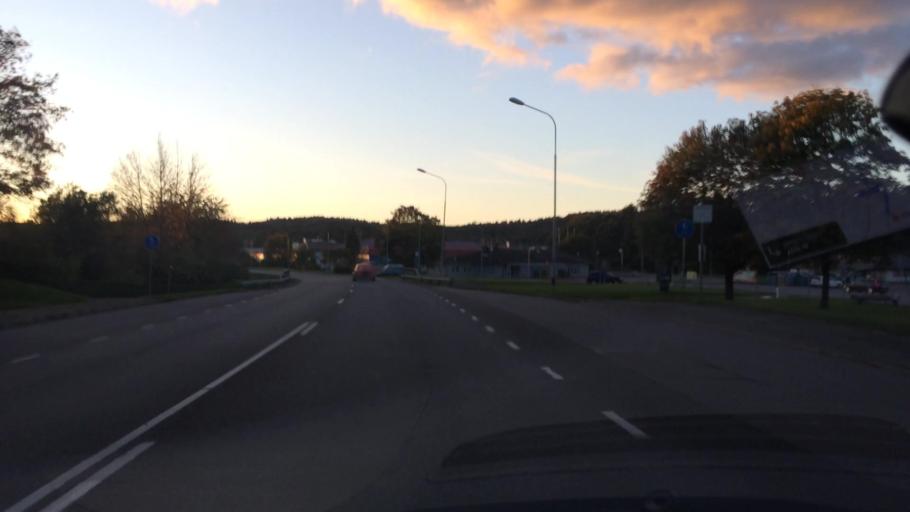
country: SE
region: Halland
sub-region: Kungsbacka Kommun
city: Kungsbacka
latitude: 57.5054
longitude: 12.0650
